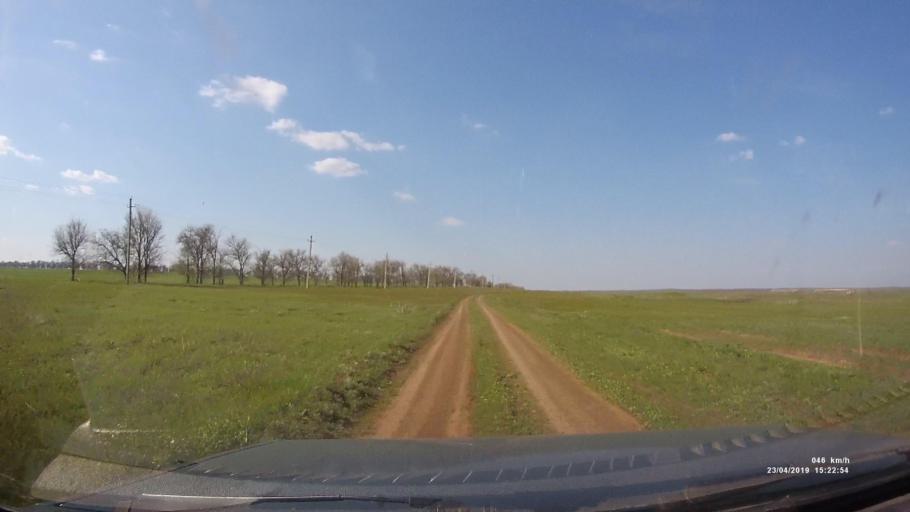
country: RU
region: Rostov
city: Remontnoye
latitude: 46.5317
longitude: 42.9697
